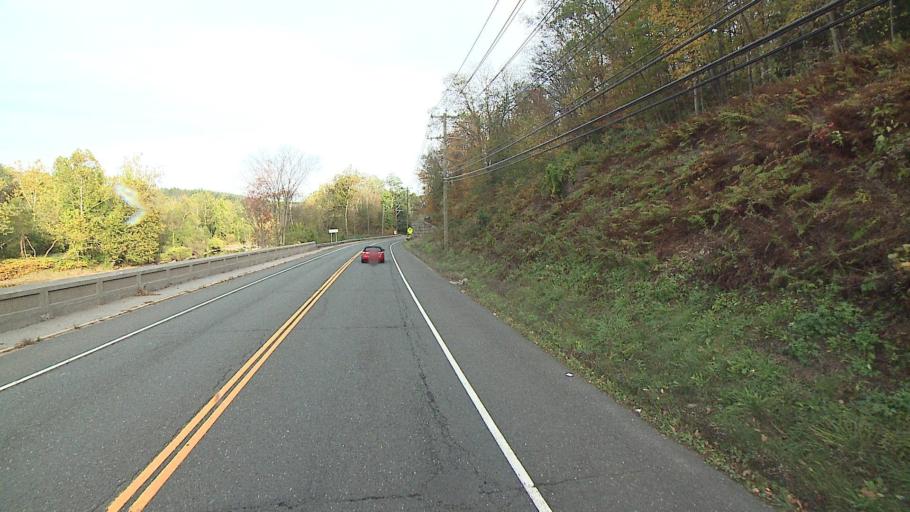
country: US
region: Connecticut
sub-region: Litchfield County
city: New Hartford Center
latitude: 41.8778
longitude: -72.9738
